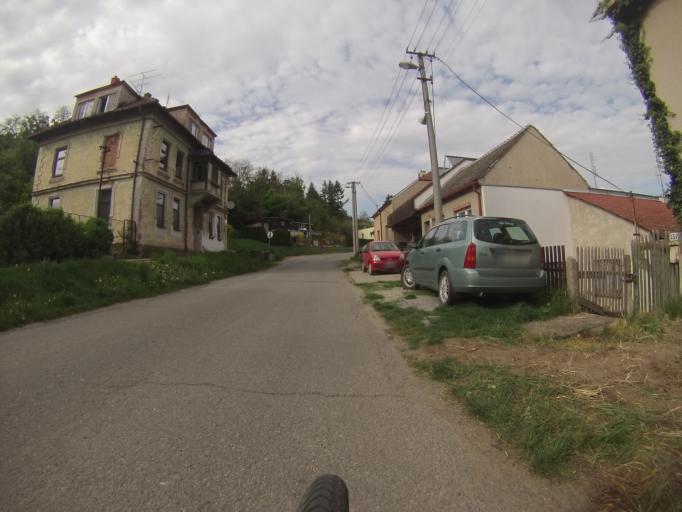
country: CZ
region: South Moravian
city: Veverska Bityska
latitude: 49.2802
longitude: 16.4389
